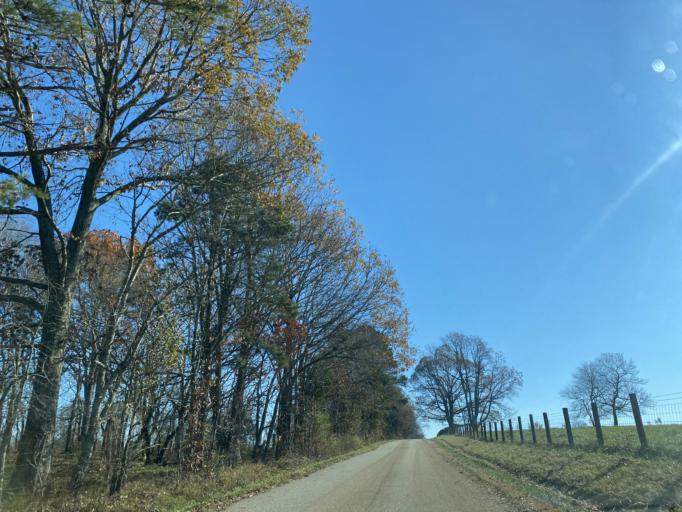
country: US
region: South Carolina
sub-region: Spartanburg County
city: Mayo
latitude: 35.1416
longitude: -81.7733
